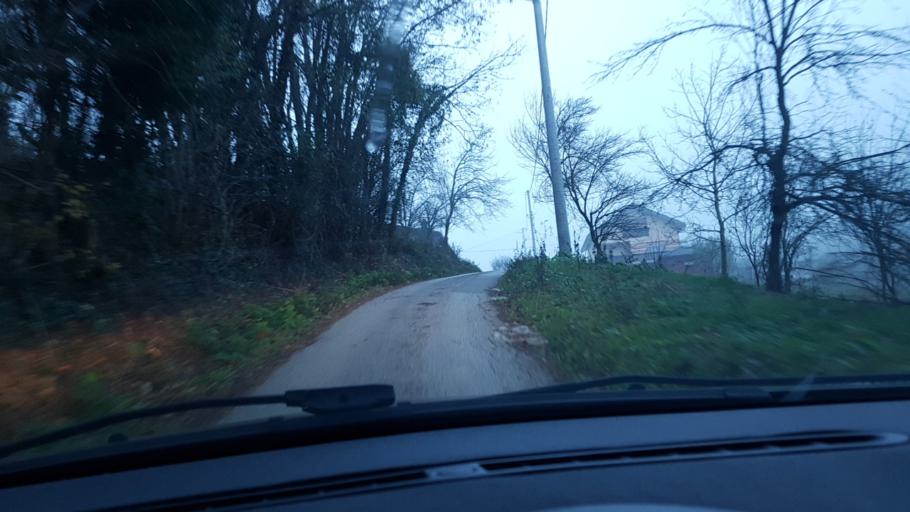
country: HR
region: Krapinsko-Zagorska
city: Pregrada
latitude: 46.2036
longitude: 15.7886
